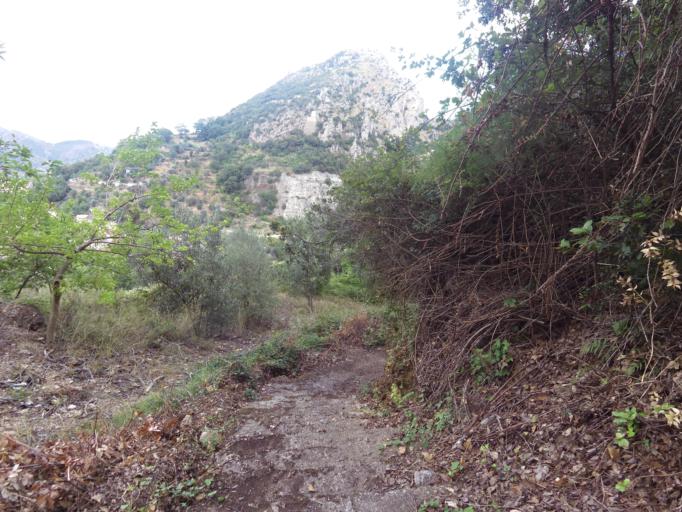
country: IT
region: Calabria
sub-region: Provincia di Reggio Calabria
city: Pazzano
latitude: 38.4740
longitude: 16.4512
